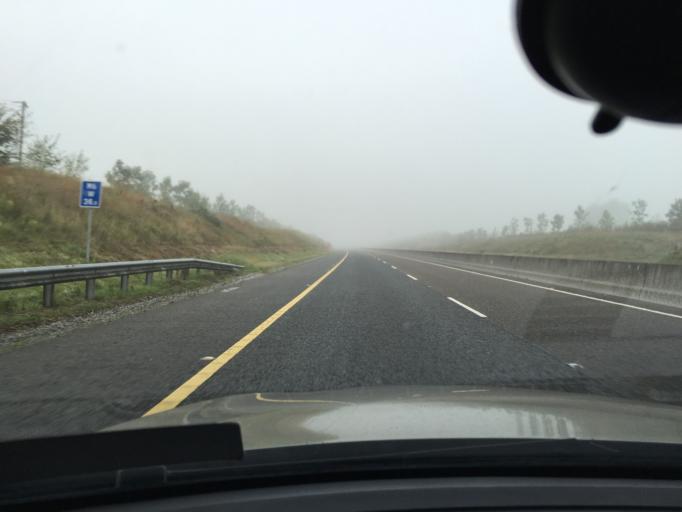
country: IE
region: Leinster
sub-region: Uibh Fhaili
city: Clara
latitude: 53.3842
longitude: -7.5828
